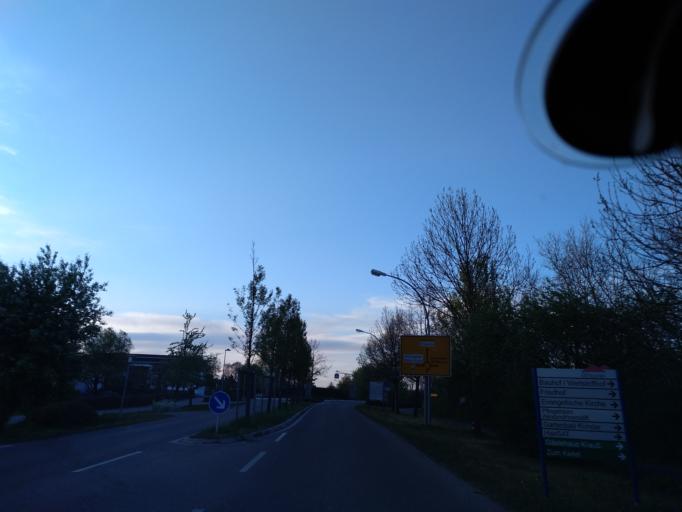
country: DE
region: Baden-Wuerttemberg
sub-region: Regierungsbezirk Stuttgart
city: Satteldorf
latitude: 49.1664
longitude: 10.0800
